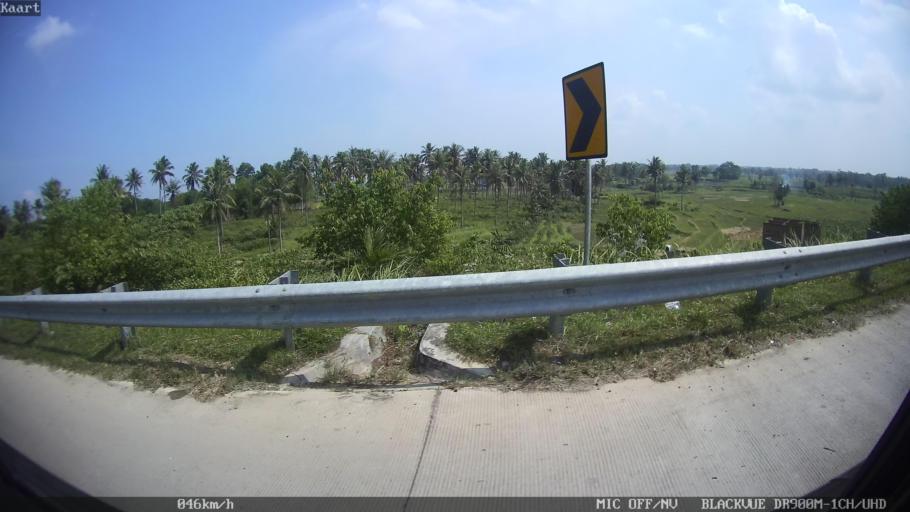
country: ID
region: Lampung
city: Natar
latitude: -5.2812
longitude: 105.1921
